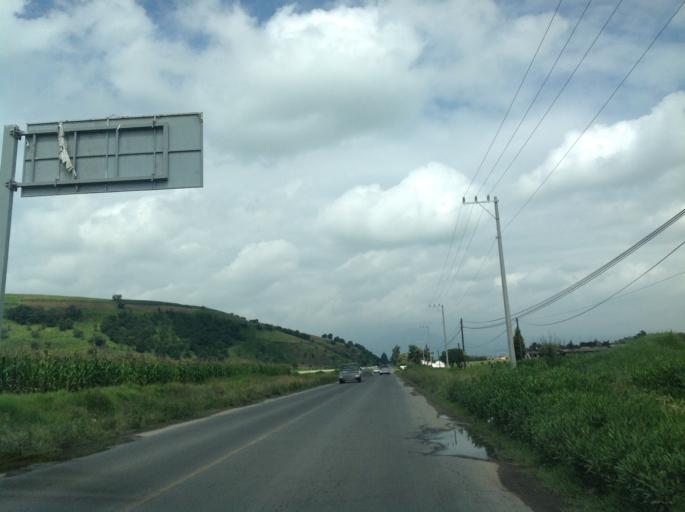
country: MX
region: Mexico
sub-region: Tenango del Valle
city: Santa Maria Jajalpa
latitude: 19.1164
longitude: -99.5429
